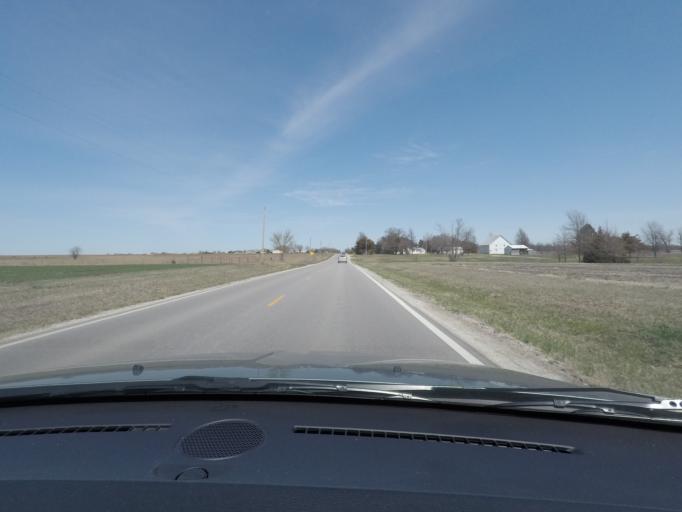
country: US
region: Kansas
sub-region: Lyon County
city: Emporia
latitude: 38.4951
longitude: -96.1708
